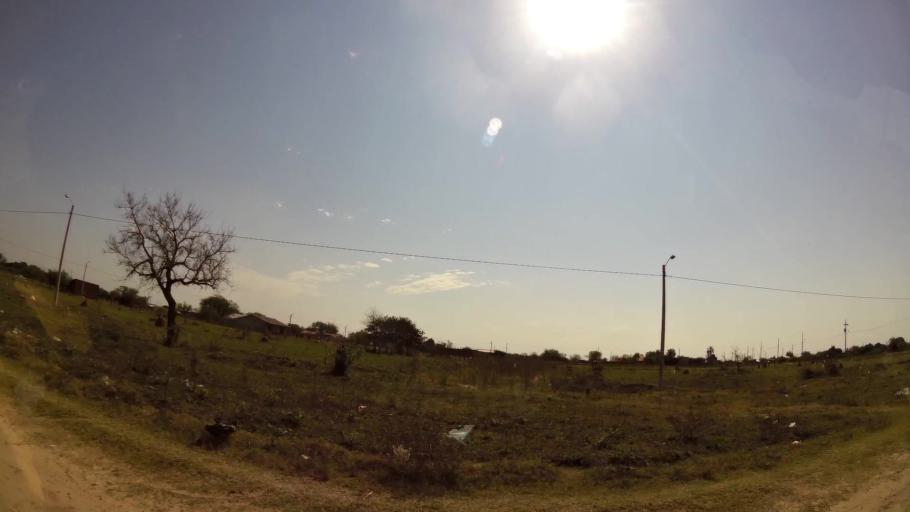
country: BO
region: Santa Cruz
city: Cotoca
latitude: -17.7209
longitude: -63.0675
